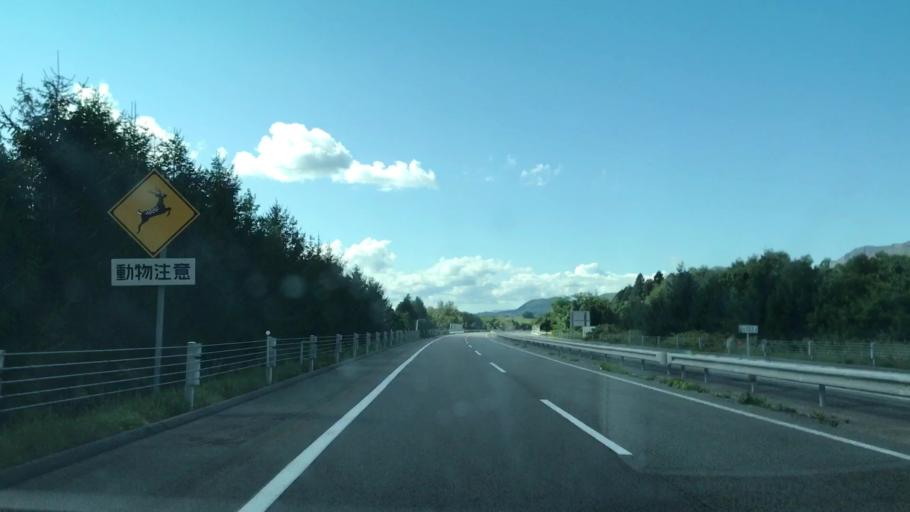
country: JP
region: Hokkaido
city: Date
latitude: 42.4873
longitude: 140.8863
